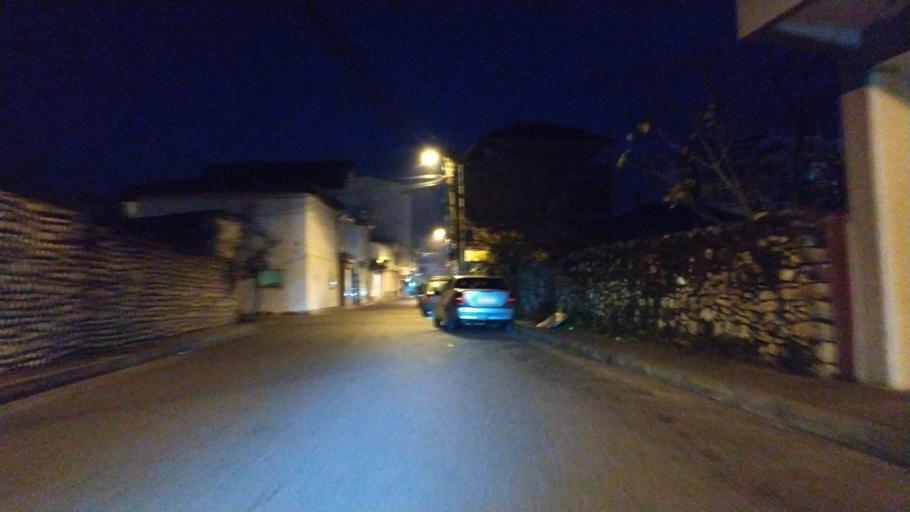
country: AL
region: Shkoder
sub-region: Rrethi i Shkodres
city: Shkoder
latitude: 42.0659
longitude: 19.5067
